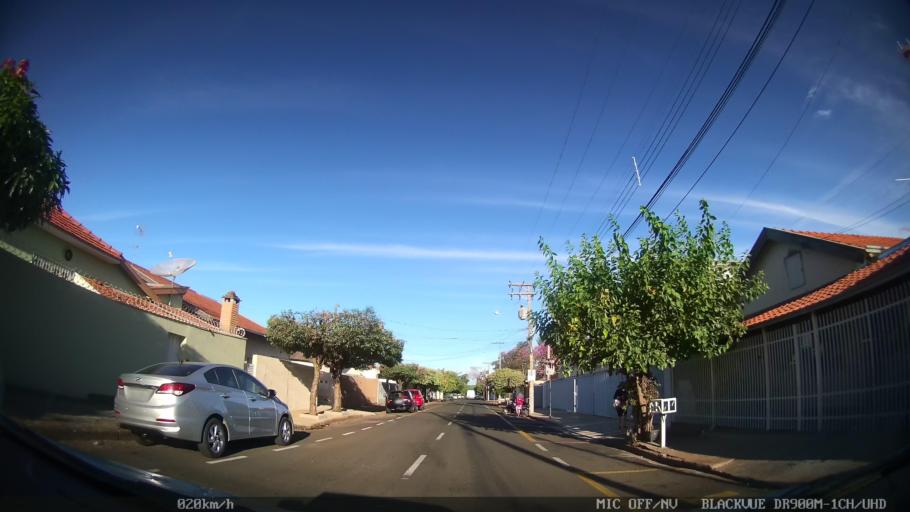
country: BR
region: Sao Paulo
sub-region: Sao Jose Do Rio Preto
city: Sao Jose do Rio Preto
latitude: -20.8316
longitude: -49.3732
